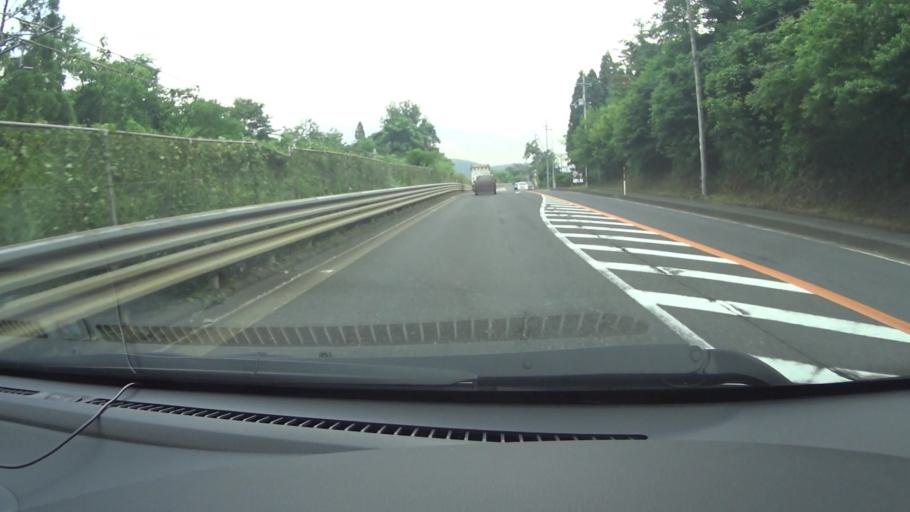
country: JP
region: Kyoto
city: Maizuru
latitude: 35.3640
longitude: 135.3180
